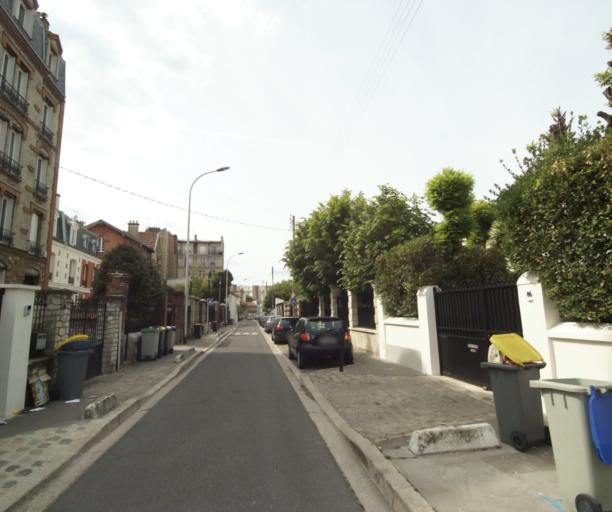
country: FR
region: Ile-de-France
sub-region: Departement des Hauts-de-Seine
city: Bois-Colombes
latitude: 48.9176
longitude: 2.2687
